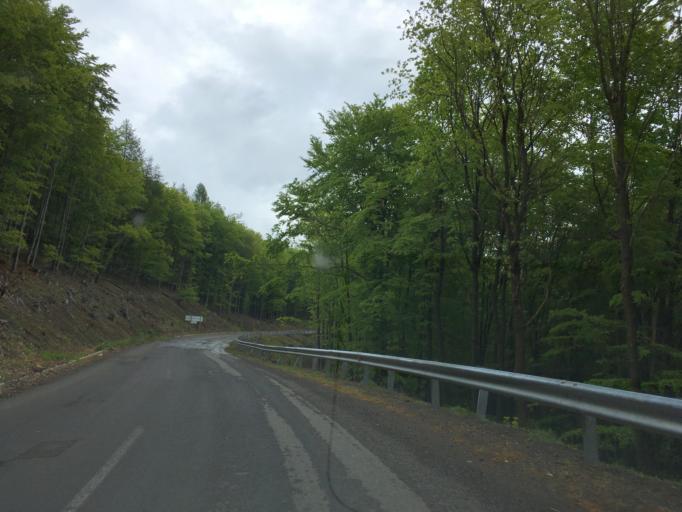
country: HU
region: Nograd
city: Batonyterenye
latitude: 47.9134
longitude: 19.8898
